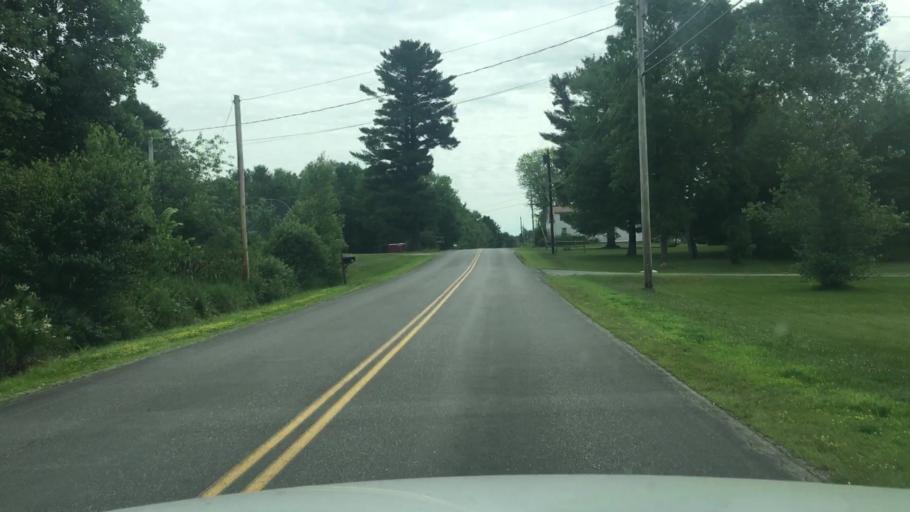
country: US
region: Maine
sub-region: Kennebec County
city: Clinton
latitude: 44.5824
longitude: -69.4868
